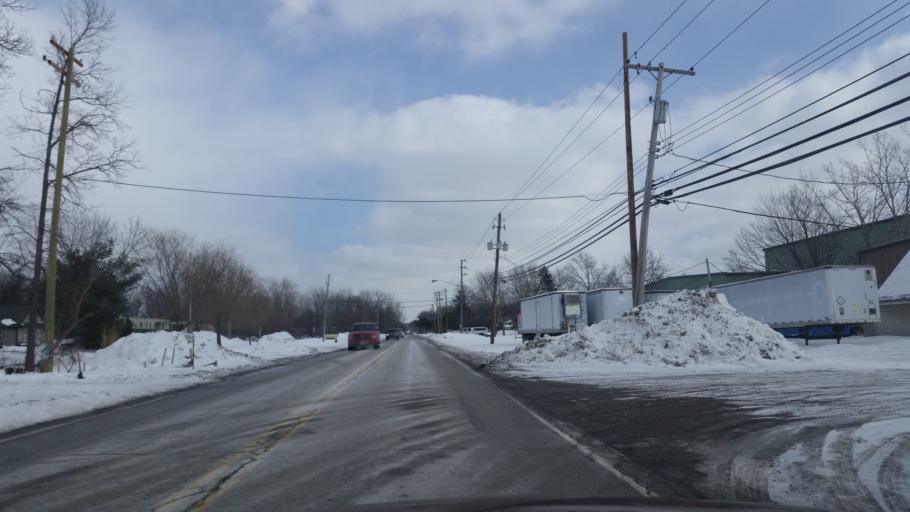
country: US
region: Ohio
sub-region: Lorain County
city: North Ridgeville
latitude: 41.4189
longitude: -81.9997
